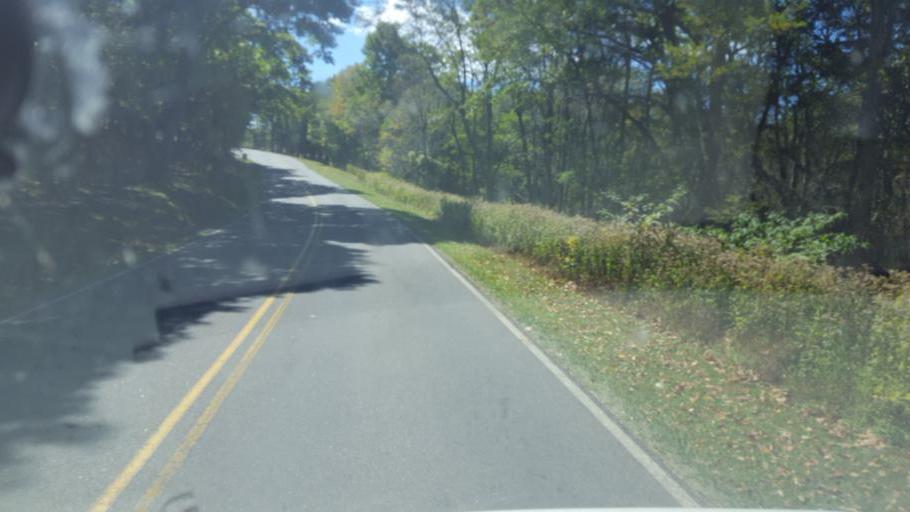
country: US
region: Virginia
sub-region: Page County
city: Stanley
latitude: 38.5192
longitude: -78.4388
